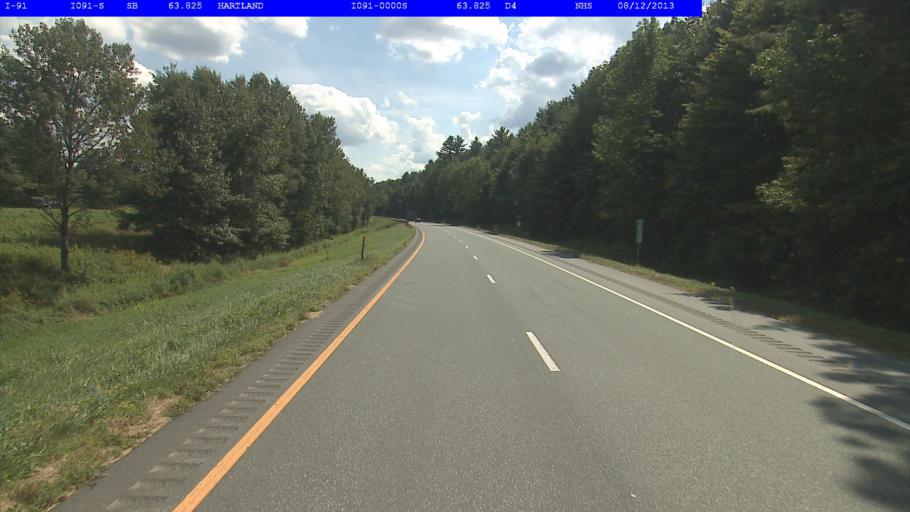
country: US
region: Vermont
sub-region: Windsor County
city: Windsor
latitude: 43.5727
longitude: -72.3865
